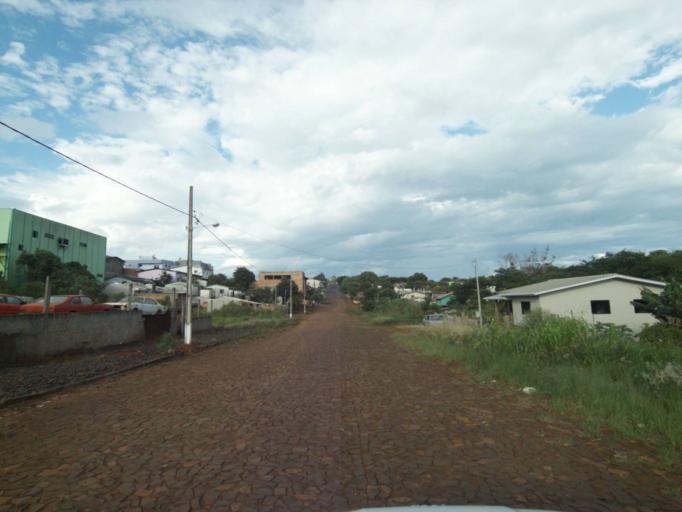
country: BR
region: Parana
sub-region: Laranjeiras Do Sul
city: Laranjeiras do Sul
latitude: -25.4937
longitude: -52.5300
